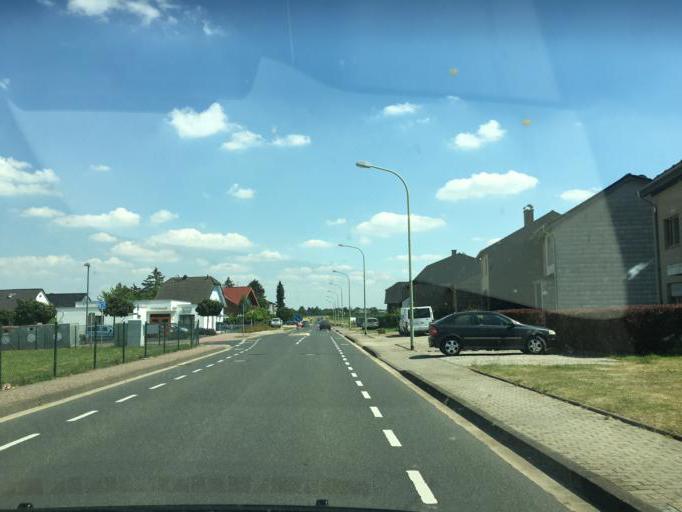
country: DE
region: North Rhine-Westphalia
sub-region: Regierungsbezirk Koln
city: Langerwehe
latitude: 50.7988
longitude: 6.4044
